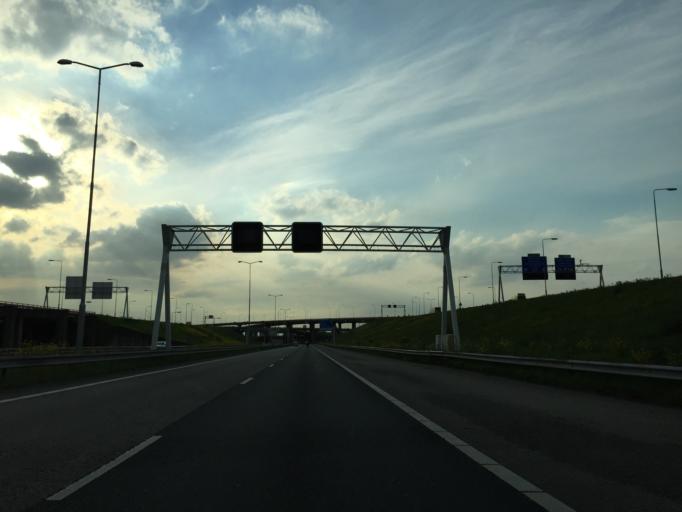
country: NL
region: South Holland
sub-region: Gemeente Den Haag
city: Ypenburg
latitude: 52.0595
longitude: 4.3827
